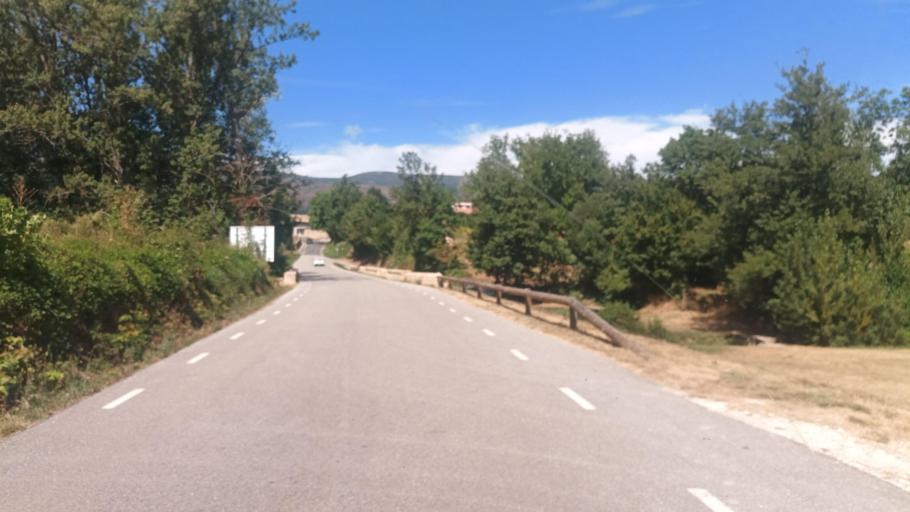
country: ES
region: Castille and Leon
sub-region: Provincia de Burgos
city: Espinosa de los Monteros
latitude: 43.0379
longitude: -3.6658
